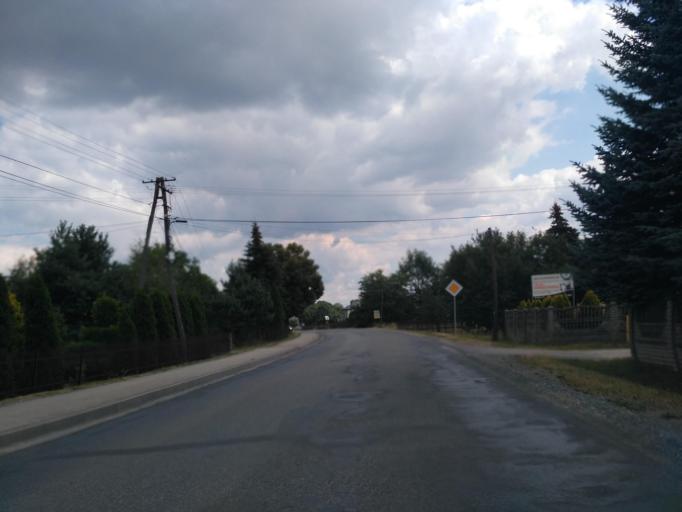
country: PL
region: Subcarpathian Voivodeship
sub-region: Powiat debicki
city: Zyrakow
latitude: 50.0541
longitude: 21.3428
